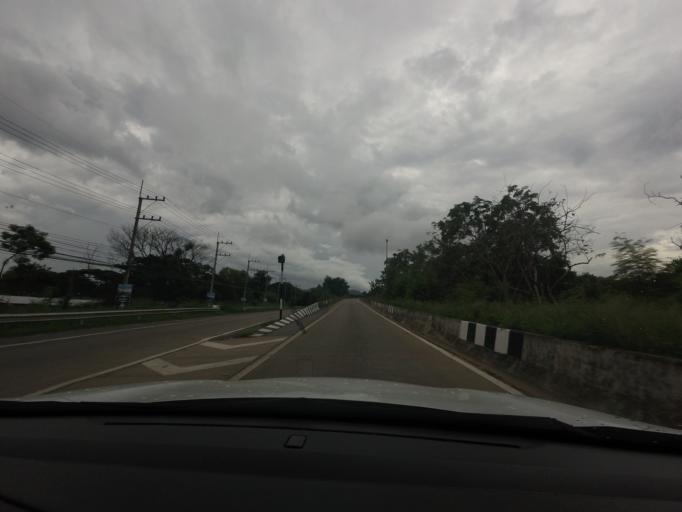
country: TH
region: Nakhon Ratchasima
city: Pak Chong
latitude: 14.6618
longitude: 101.4066
